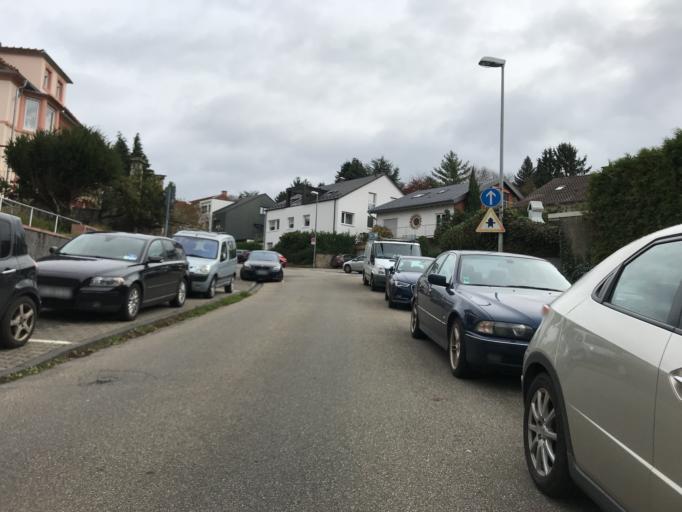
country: DE
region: Rheinland-Pfalz
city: Mainz
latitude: 49.9634
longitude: 8.2829
